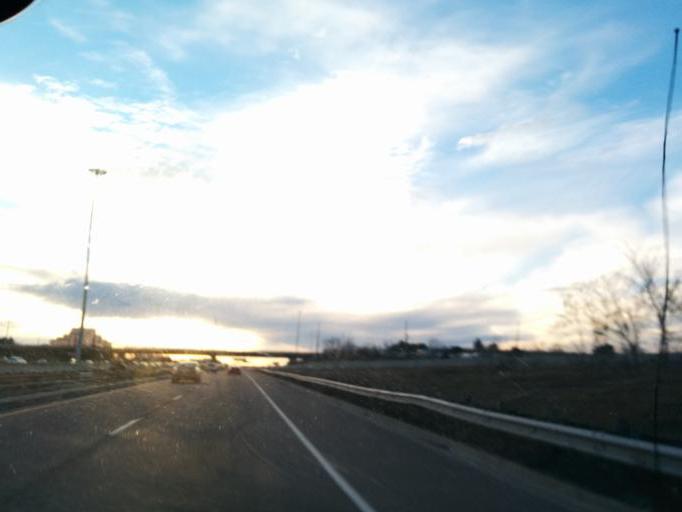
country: CA
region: Ontario
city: Etobicoke
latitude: 43.6703
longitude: -79.5888
